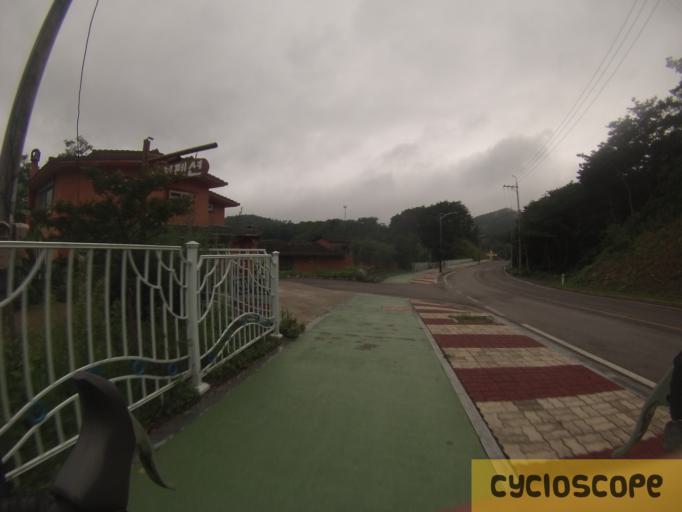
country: KR
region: Chungcheongnam-do
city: Yesan
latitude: 36.7459
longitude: 126.8637
